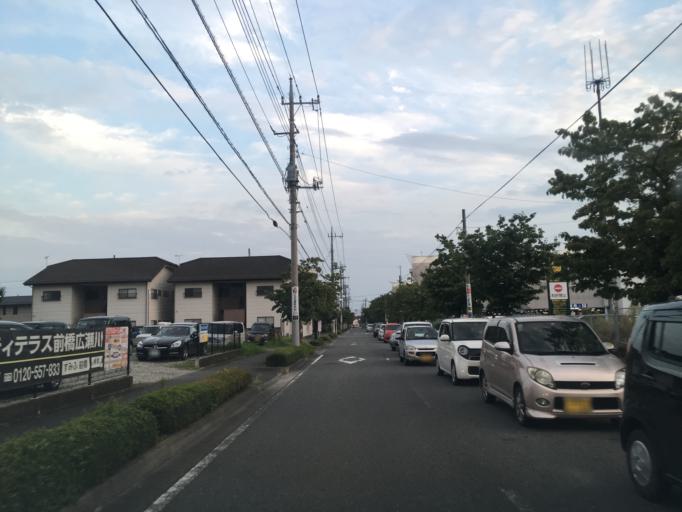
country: JP
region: Gunma
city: Maebashi-shi
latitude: 36.3799
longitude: 139.0799
